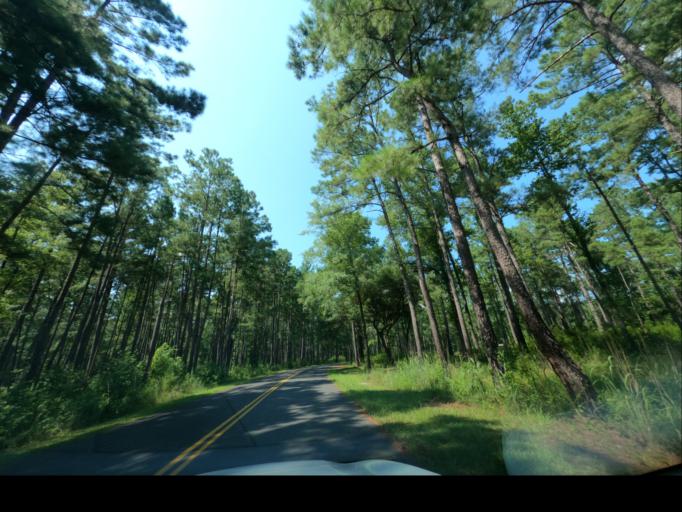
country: US
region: South Carolina
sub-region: Richland County
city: Gadsden
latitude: 33.8344
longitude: -80.8286
